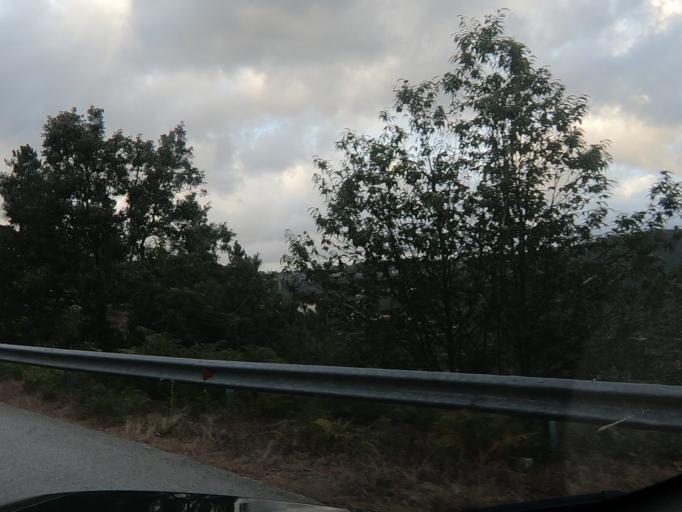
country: PT
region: Vila Real
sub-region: Santa Marta de Penaguiao
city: Santa Marta de Penaguiao
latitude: 41.2549
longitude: -7.8564
